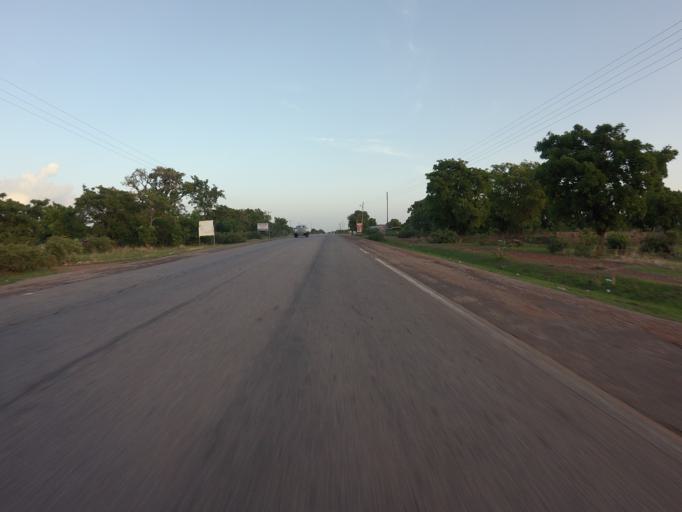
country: GH
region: Upper East
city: Navrongo
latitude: 10.9470
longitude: -1.0940
